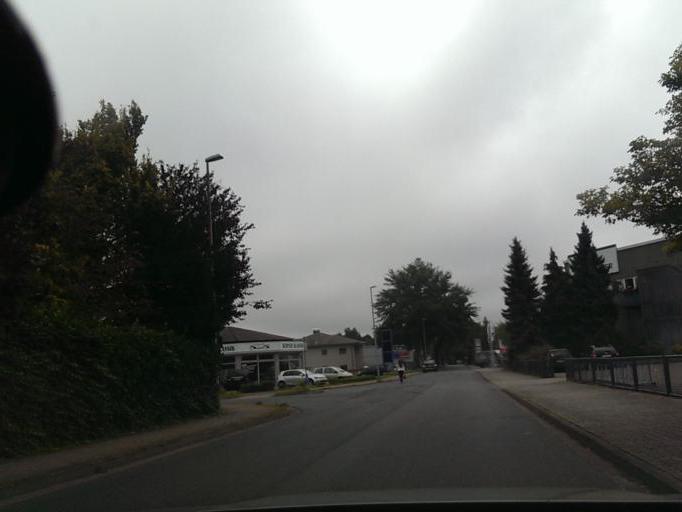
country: DE
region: Lower Saxony
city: Isernhagen Farster Bauerschaft
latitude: 52.4292
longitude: 9.8345
